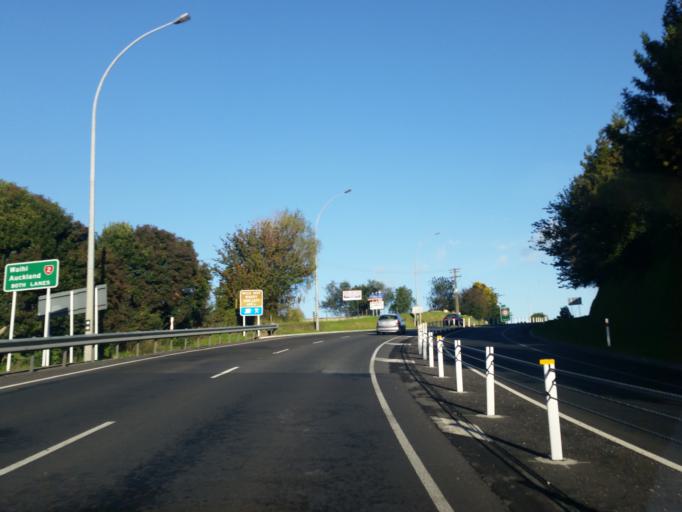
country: NZ
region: Bay of Plenty
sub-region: Tauranga City
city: Tauranga
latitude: -37.6950
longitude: 176.1178
